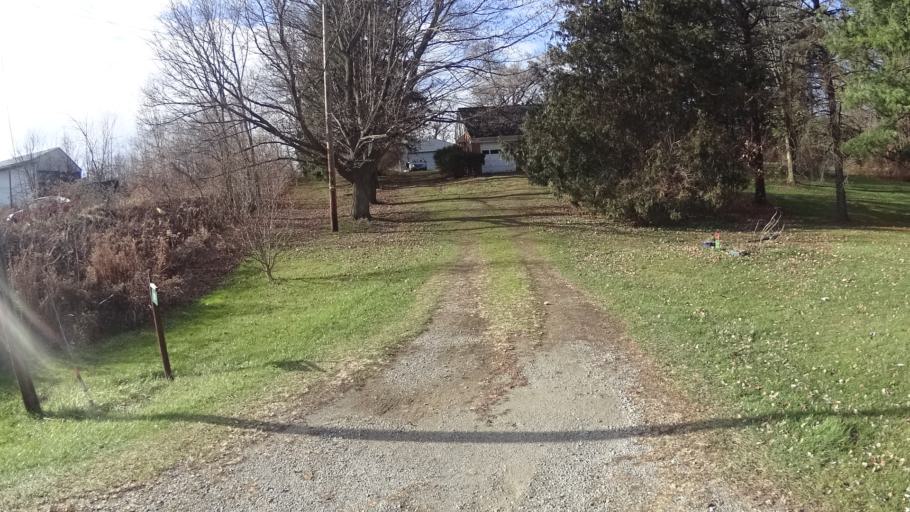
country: US
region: Ohio
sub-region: Lorain County
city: Camden
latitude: 41.2688
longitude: -82.3035
